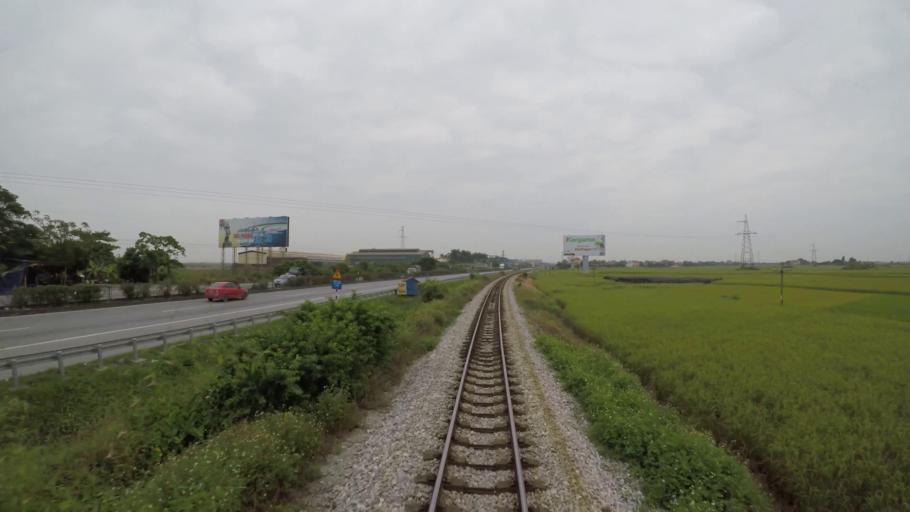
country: VN
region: Hai Duong
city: Phu Thai
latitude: 20.9496
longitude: 106.5338
